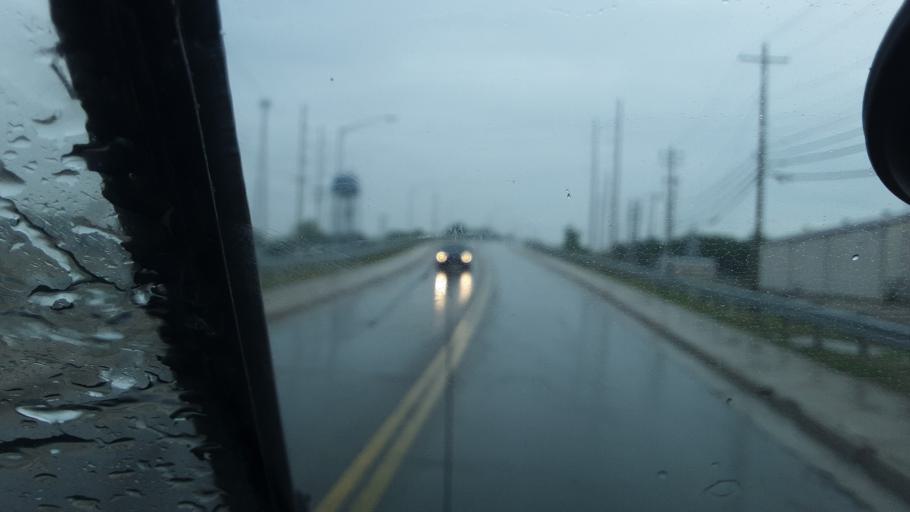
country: US
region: Ohio
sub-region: Williams County
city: Montpelier
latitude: 41.5770
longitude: -84.6071
